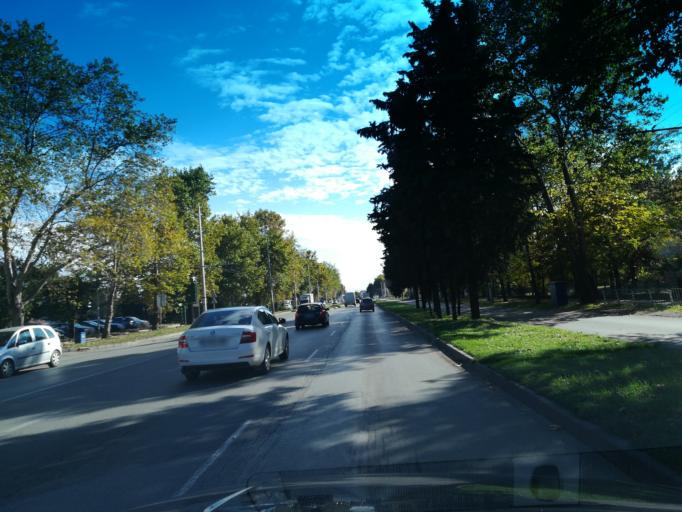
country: BG
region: Stara Zagora
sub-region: Obshtina Stara Zagora
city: Stara Zagora
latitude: 42.4071
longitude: 25.6407
